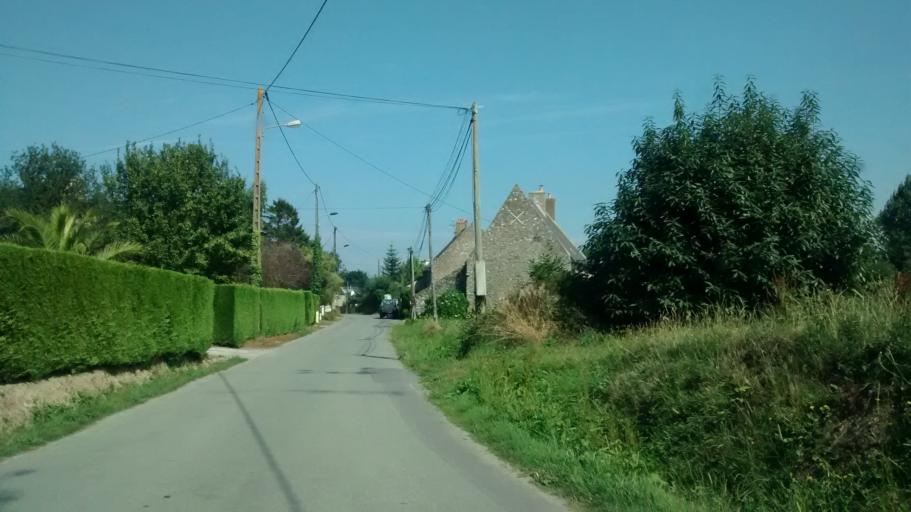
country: FR
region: Brittany
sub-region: Departement d'Ille-et-Vilaine
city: Saint-Coulomb
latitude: 48.6846
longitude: -1.8966
